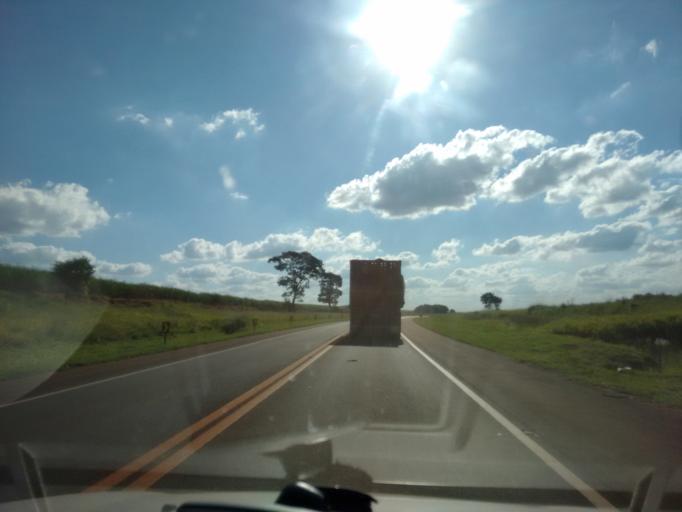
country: BR
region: Sao Paulo
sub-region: Americo Brasiliense
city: Americo Brasiliense
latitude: -21.6206
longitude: -48.0223
